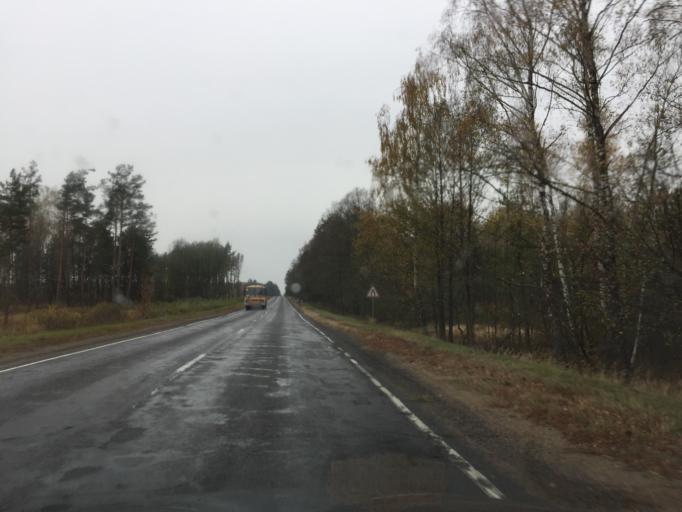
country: BY
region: Gomel
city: Karma
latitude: 53.3317
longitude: 30.7844
